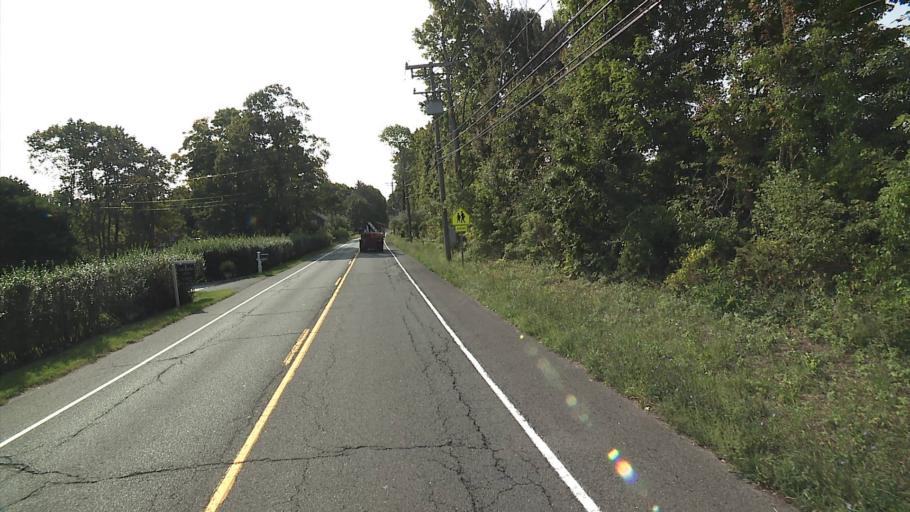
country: US
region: Connecticut
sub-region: Fairfield County
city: Bethel
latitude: 41.3152
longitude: -73.3514
